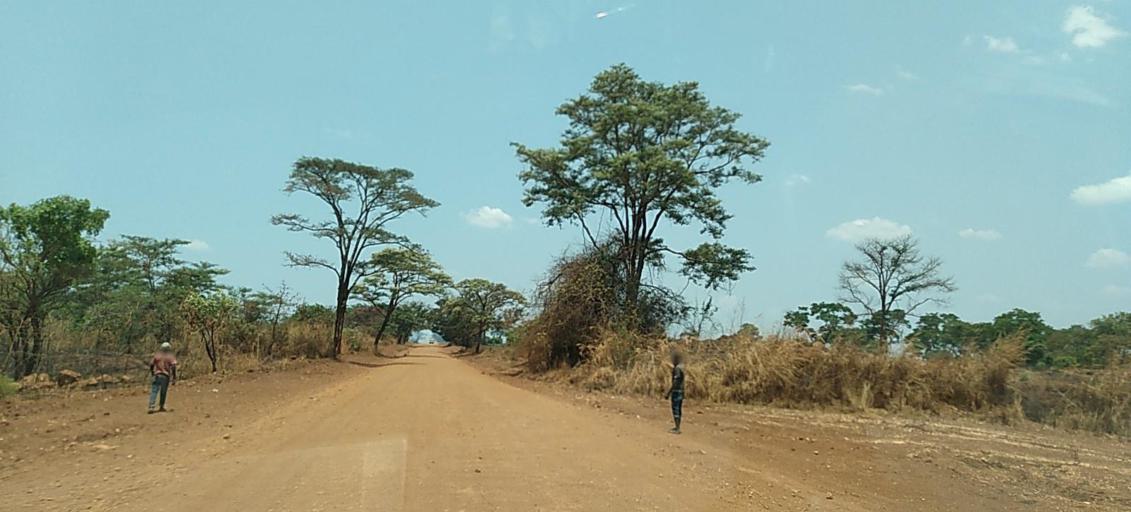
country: ZM
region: Copperbelt
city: Mpongwe
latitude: -13.5176
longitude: 27.9793
